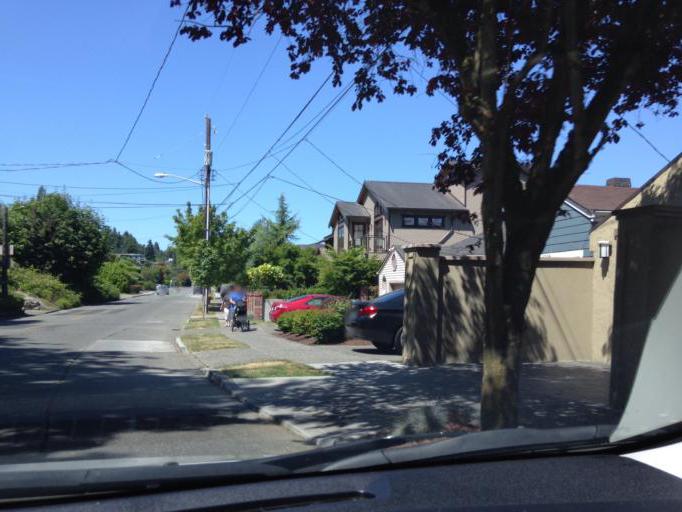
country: US
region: Washington
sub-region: King County
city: Seattle
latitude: 47.5927
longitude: -122.2878
